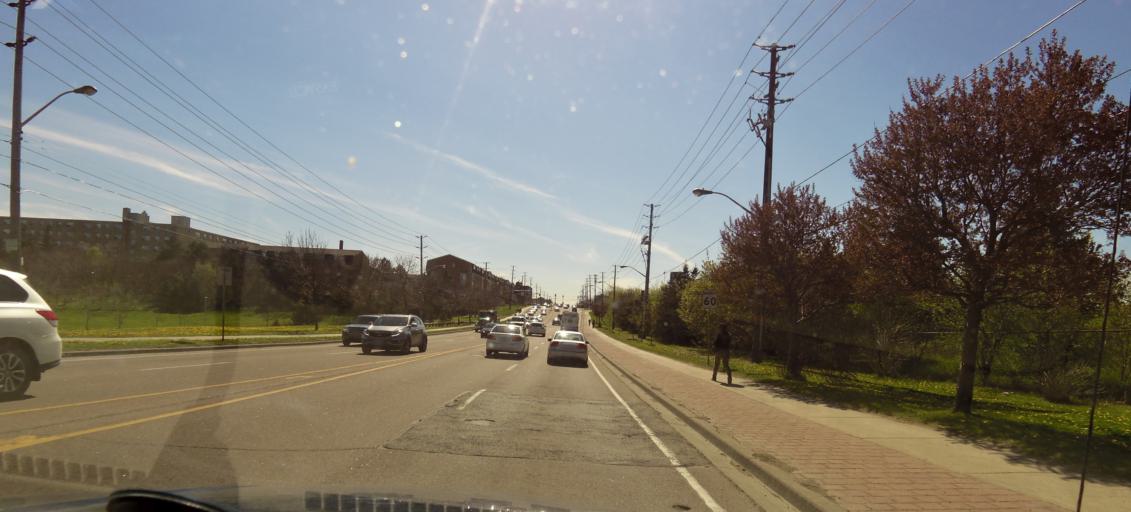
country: CA
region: Ontario
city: Concord
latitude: 43.7515
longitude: -79.5457
